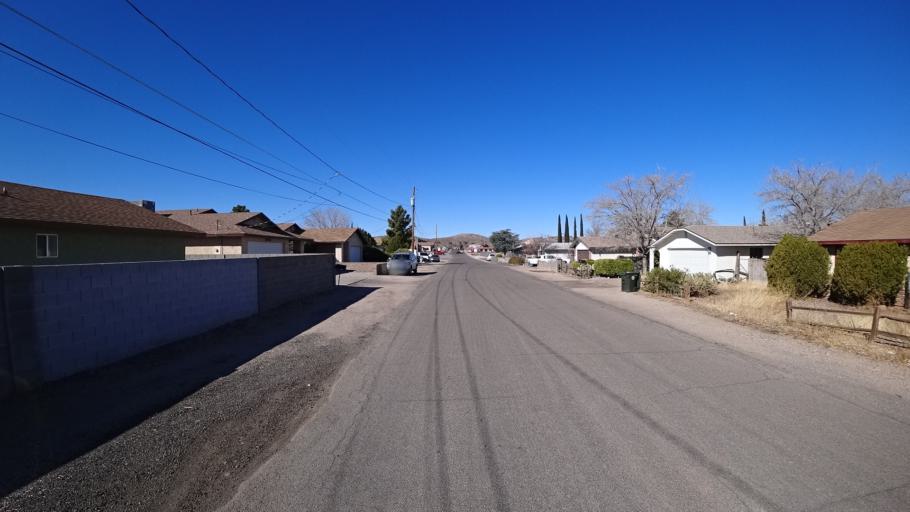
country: US
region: Arizona
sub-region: Mohave County
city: Kingman
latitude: 35.2060
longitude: -114.0317
